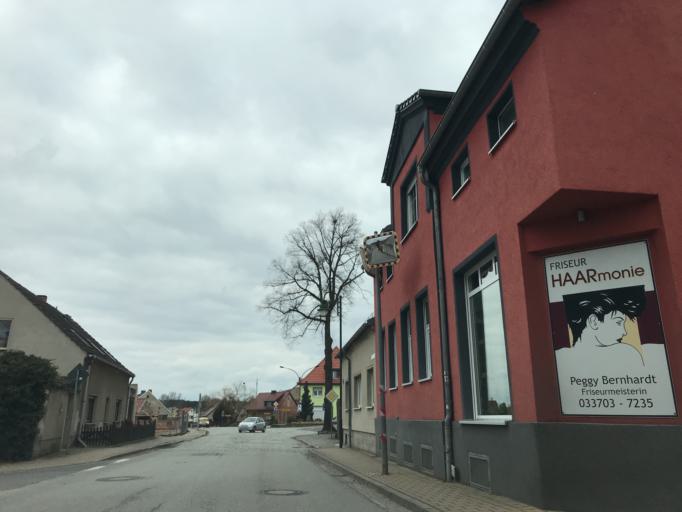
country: DE
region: Brandenburg
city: Sperenberg
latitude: 52.1411
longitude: 13.3651
